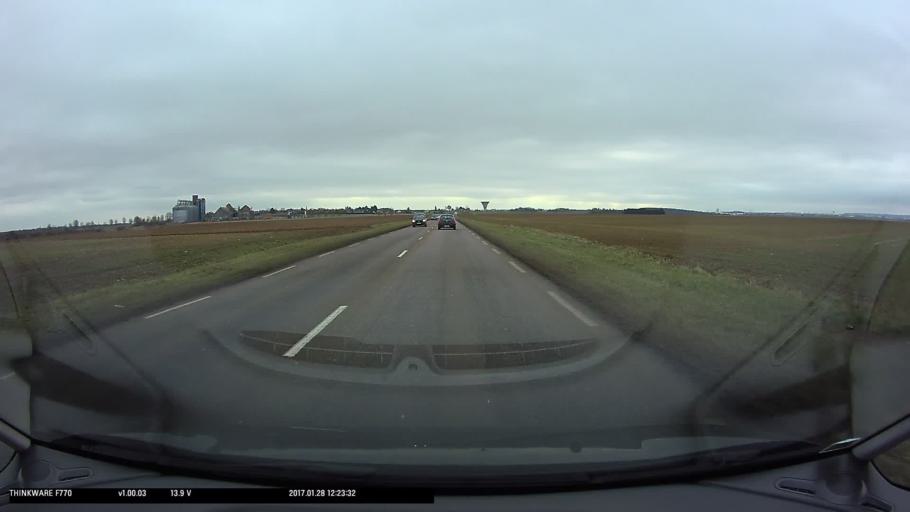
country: FR
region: Ile-de-France
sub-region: Departement du Val-d'Oise
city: Osny
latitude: 49.0959
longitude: 2.0501
